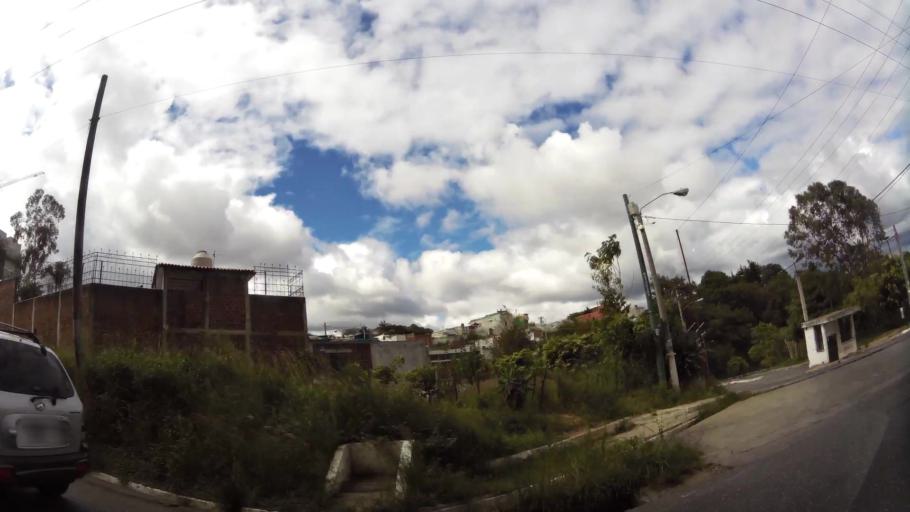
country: GT
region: Guatemala
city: Guatemala City
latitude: 14.6738
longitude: -90.5511
